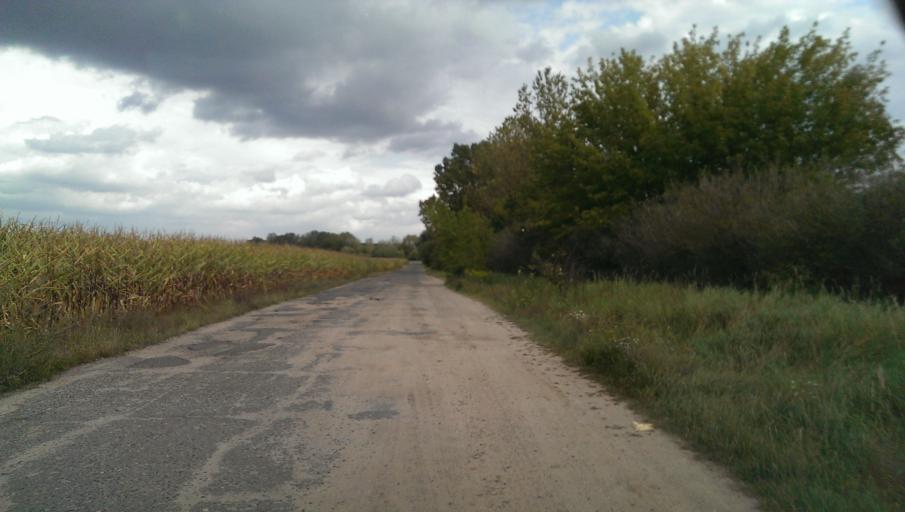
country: DE
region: Brandenburg
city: Rangsdorf
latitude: 52.2916
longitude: 13.4746
